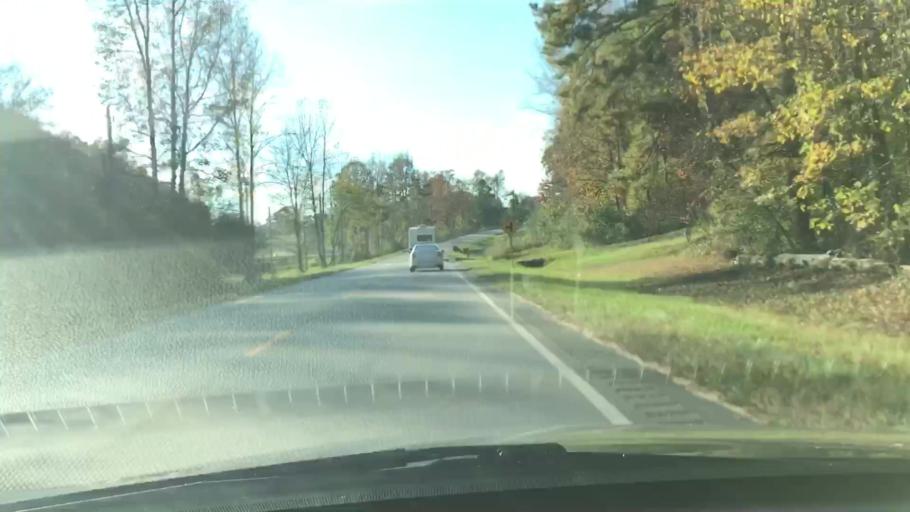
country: US
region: Alabama
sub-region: Cleburne County
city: Heflin
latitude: 33.6501
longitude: -85.5466
